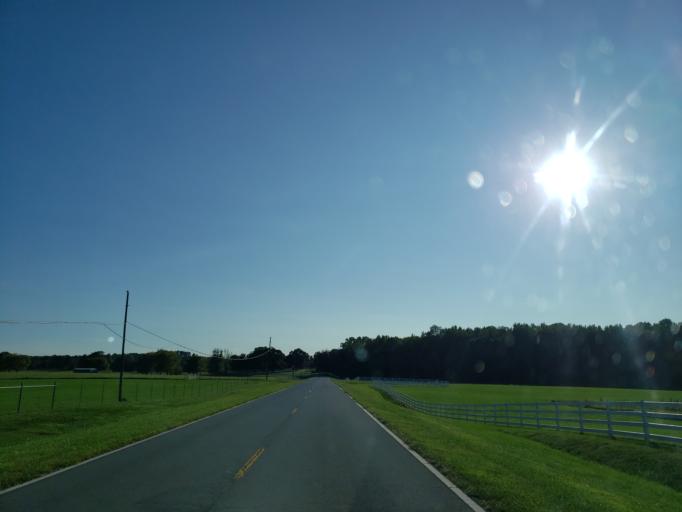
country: US
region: Georgia
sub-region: Bartow County
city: Rydal
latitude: 34.3150
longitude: -84.7701
